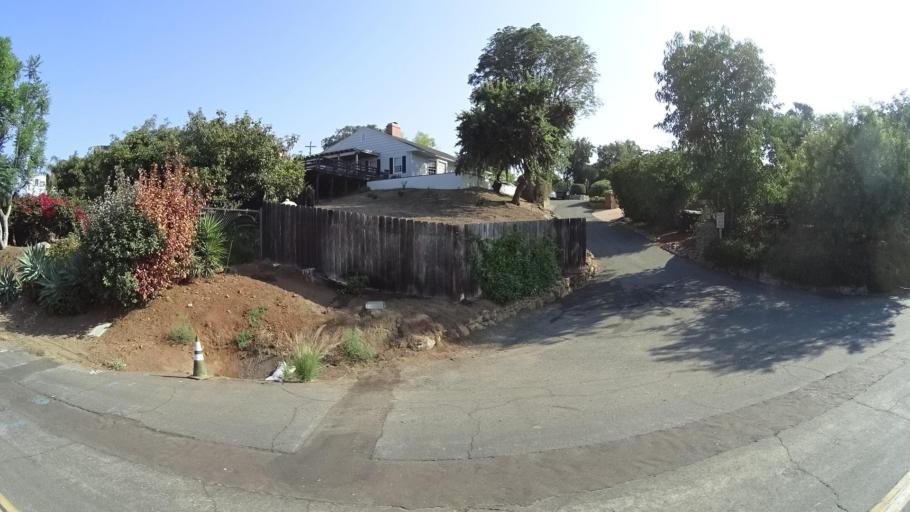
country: US
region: California
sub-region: San Diego County
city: Vista
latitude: 33.2298
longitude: -117.2147
